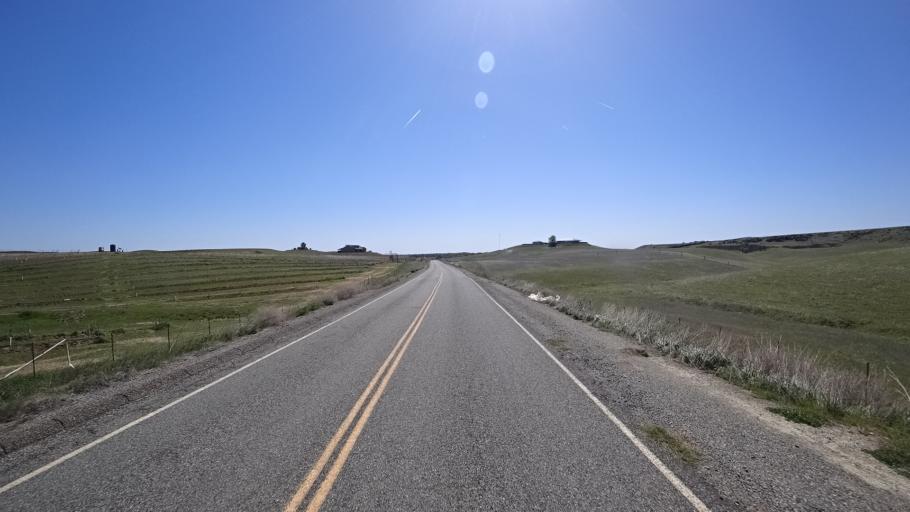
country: US
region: California
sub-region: Glenn County
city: Orland
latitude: 39.8296
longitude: -122.3395
